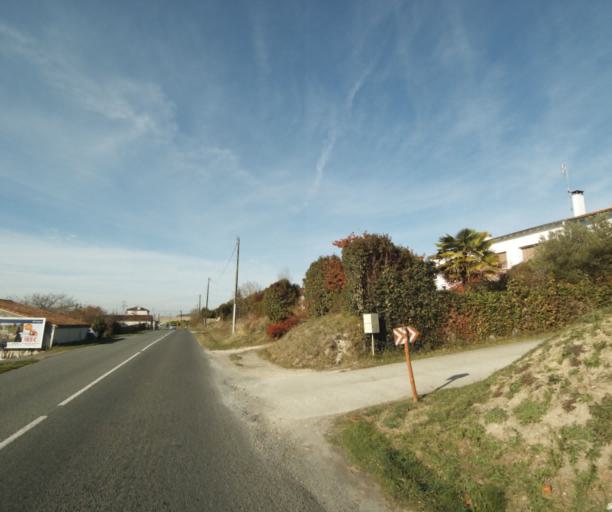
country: FR
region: Poitou-Charentes
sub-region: Departement de la Charente-Maritime
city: Chaniers
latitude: 45.7237
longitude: -0.5708
